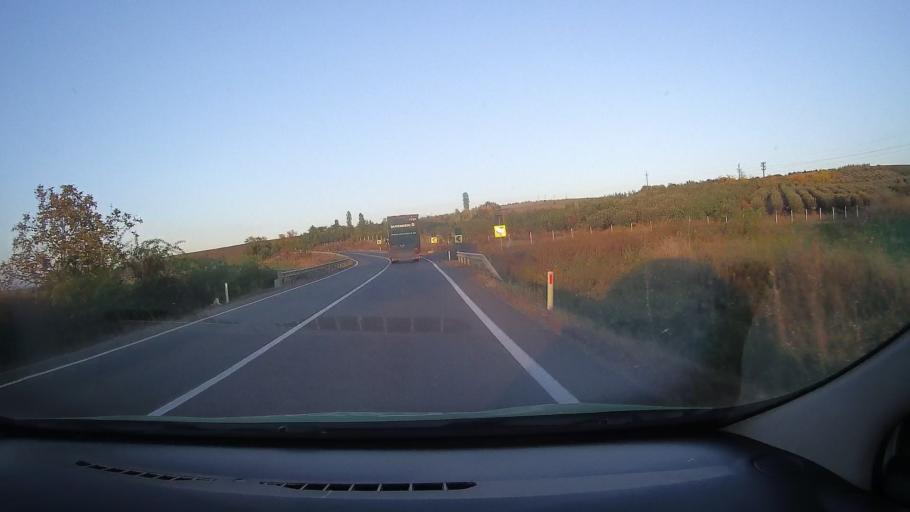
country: RO
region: Bihor
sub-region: Comuna Sacueni
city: Cadea
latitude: 47.3116
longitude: 22.0394
